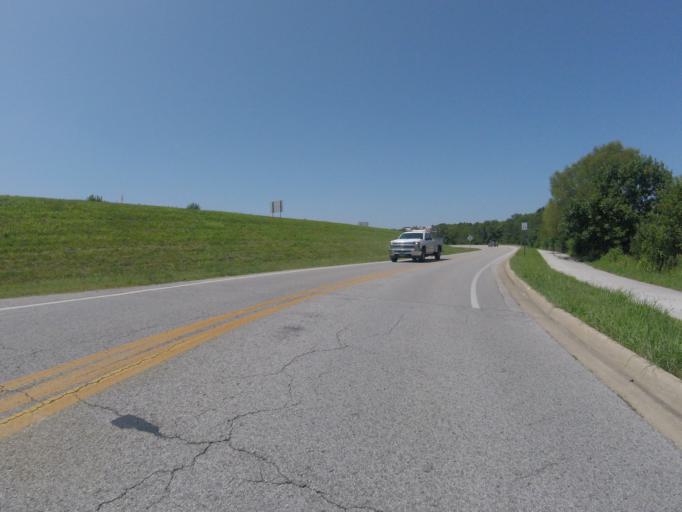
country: US
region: Arkansas
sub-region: Washington County
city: Johnson
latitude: 36.1071
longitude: -94.1807
